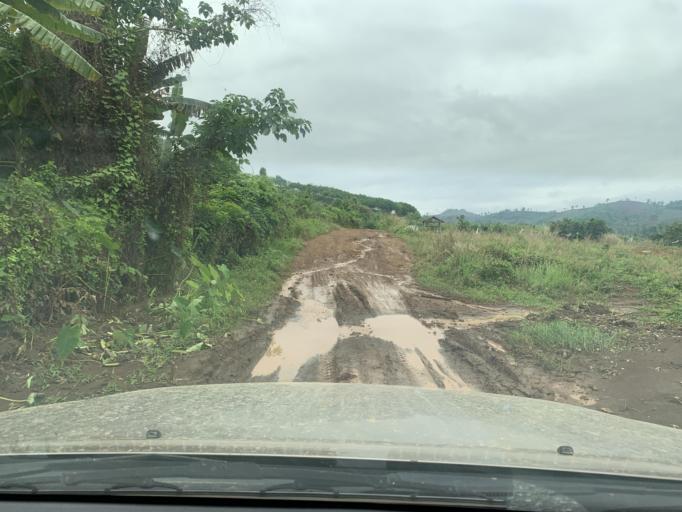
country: TH
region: Nan
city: Mae Charim
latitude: 18.4047
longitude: 101.4382
